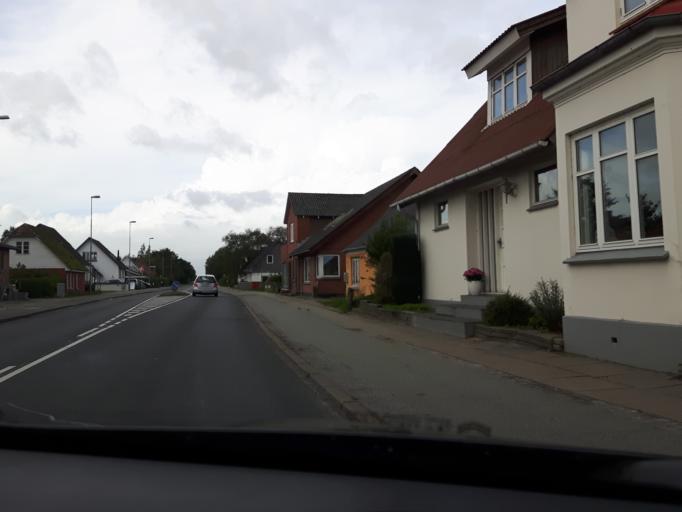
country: DK
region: North Denmark
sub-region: Jammerbugt Kommune
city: Brovst
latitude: 57.1092
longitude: 9.5830
